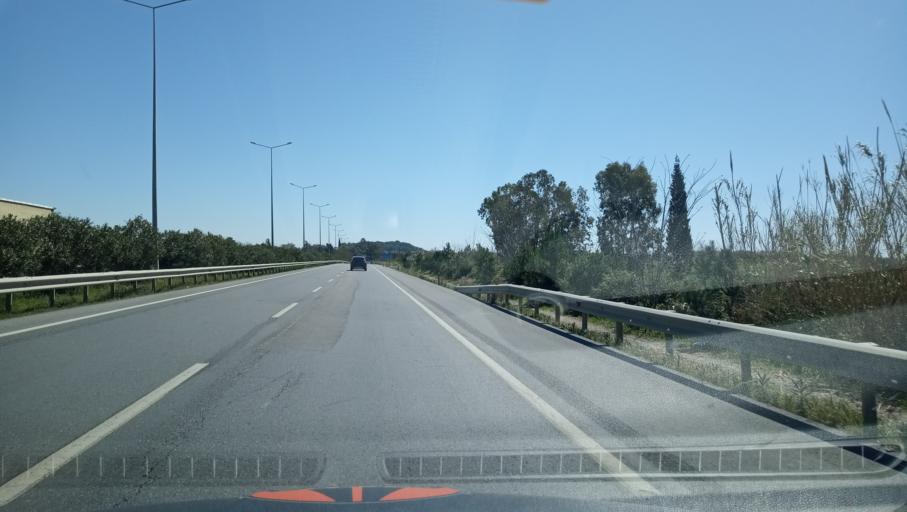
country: TR
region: Antalya
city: Tasagil
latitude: 36.8400
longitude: 31.3073
